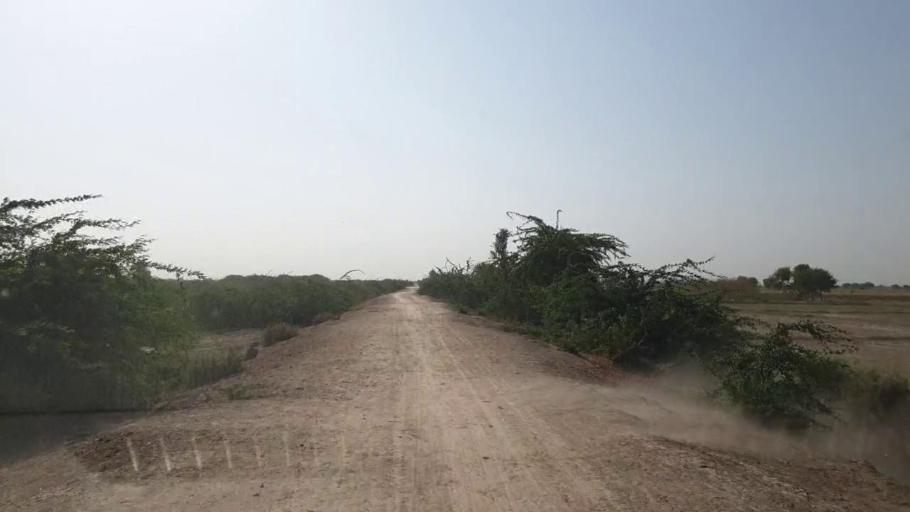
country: PK
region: Sindh
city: Kadhan
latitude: 24.5747
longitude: 69.0815
